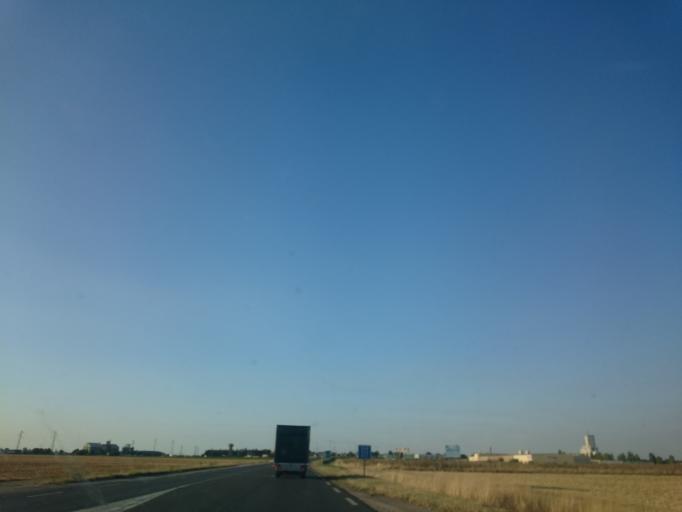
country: FR
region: Centre
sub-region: Departement d'Eure-et-Loir
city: Toury
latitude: 48.1794
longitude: 1.9266
